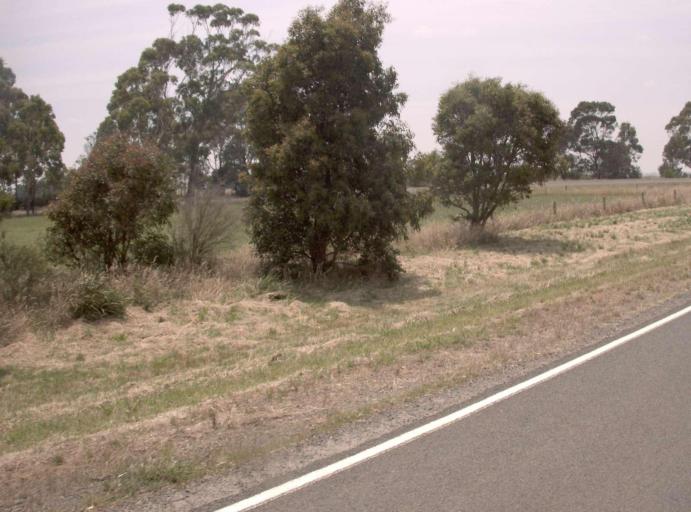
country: AU
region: Victoria
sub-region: Latrobe
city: Traralgon
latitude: -38.2424
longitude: 146.6301
